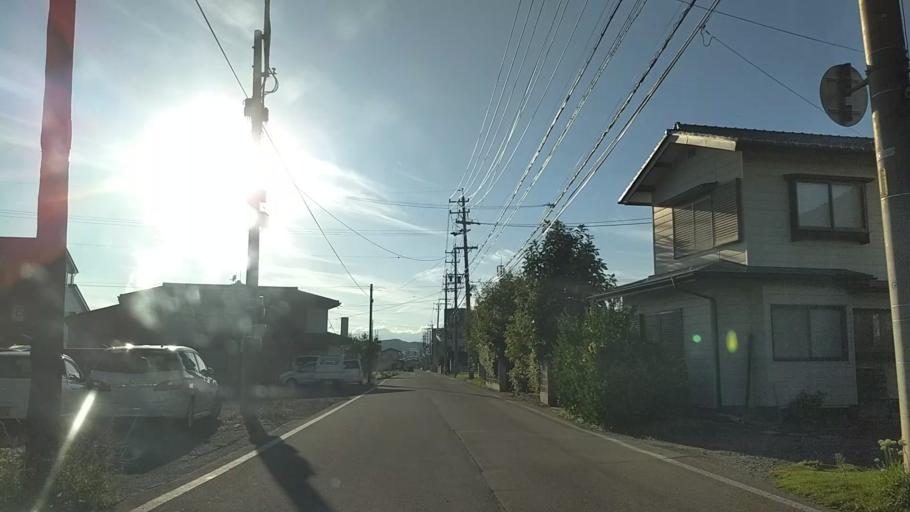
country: JP
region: Nagano
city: Nagano-shi
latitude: 36.6095
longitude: 138.2040
